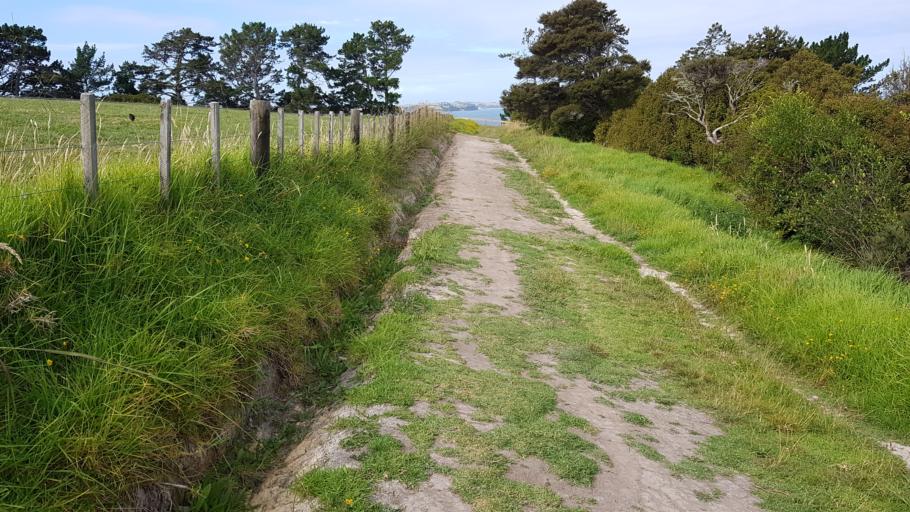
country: NZ
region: Auckland
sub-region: Auckland
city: Rothesay Bay
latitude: -36.6653
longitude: 174.7475
